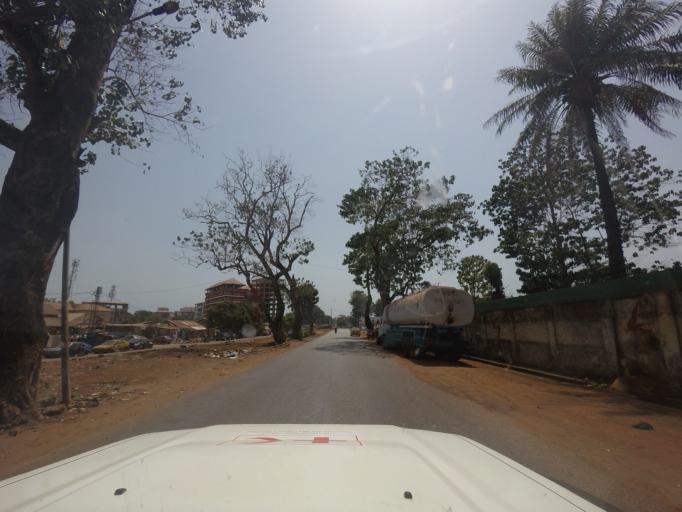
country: GN
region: Conakry
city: Camayenne
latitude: 9.5184
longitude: -13.6975
